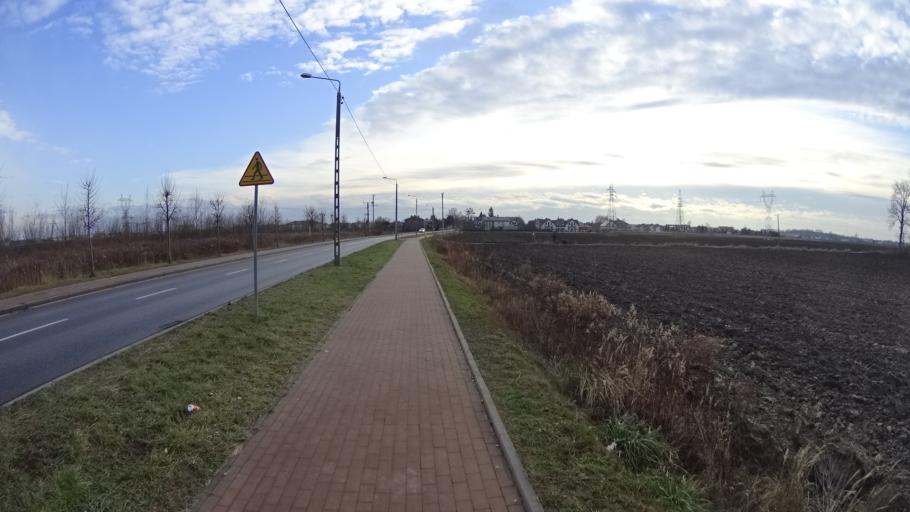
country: PL
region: Masovian Voivodeship
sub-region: Powiat warszawski zachodni
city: Ozarow Mazowiecki
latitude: 52.2290
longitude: 20.8024
